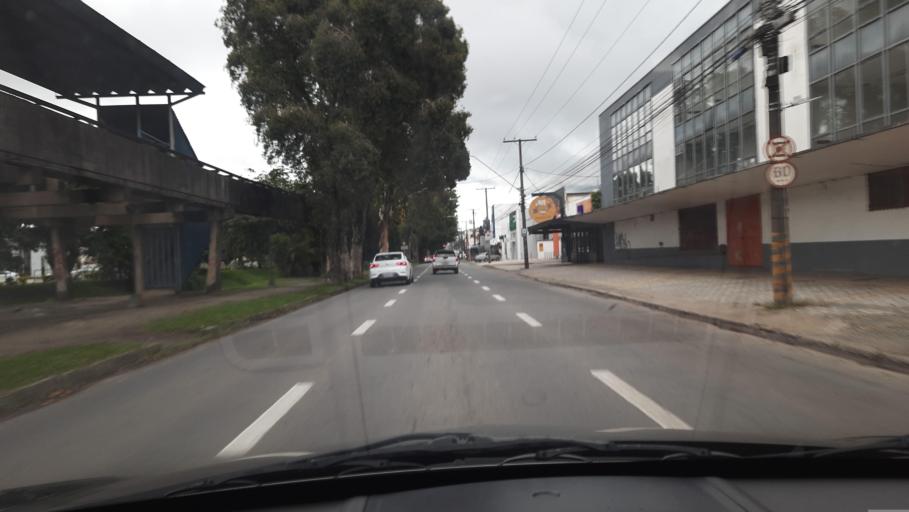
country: BR
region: Minas Gerais
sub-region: Pocos De Caldas
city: Pocos de Caldas
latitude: -21.7853
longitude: -46.5831
